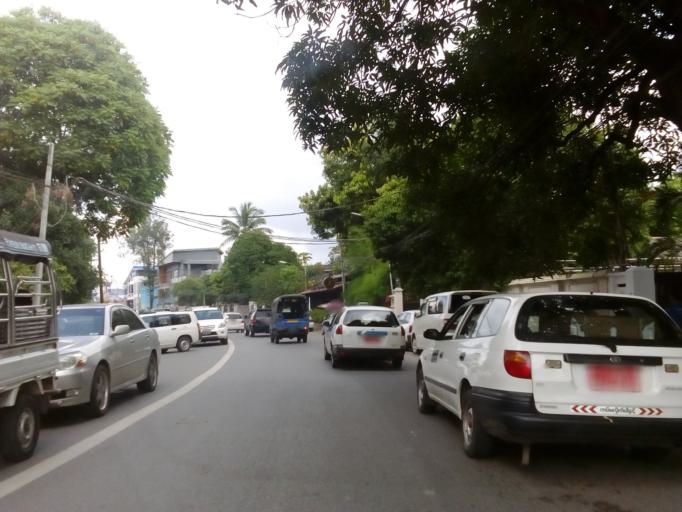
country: MM
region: Yangon
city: Yangon
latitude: 16.8162
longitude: 96.1580
